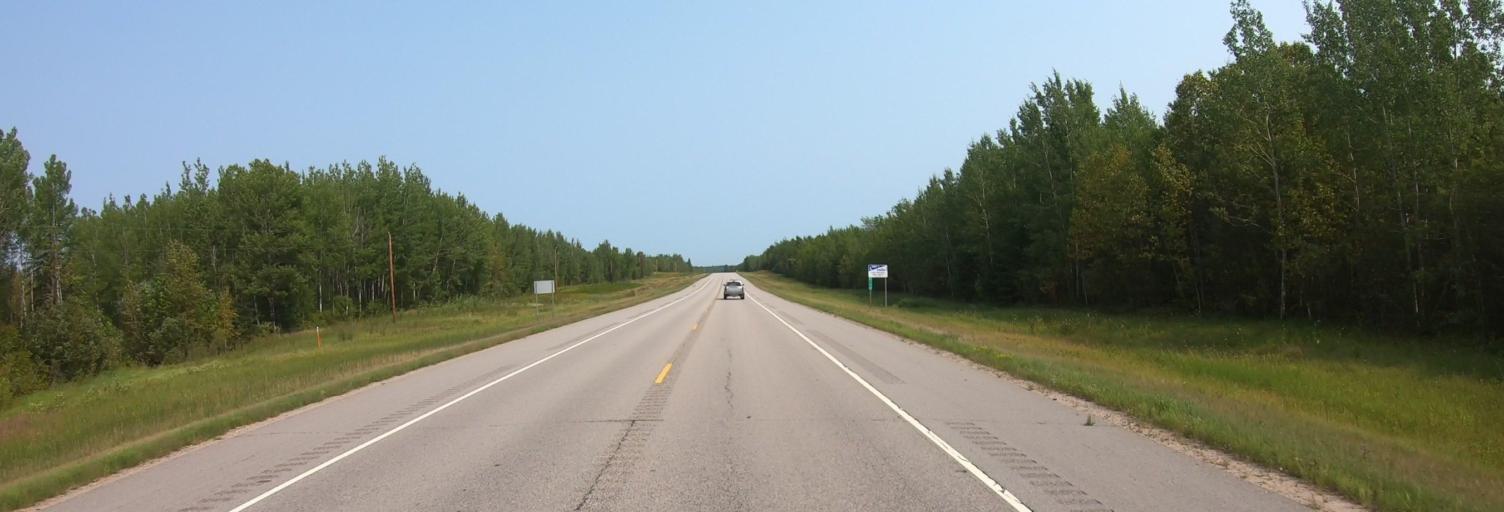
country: CA
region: Ontario
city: Fort Frances
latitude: 48.3049
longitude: -92.9678
